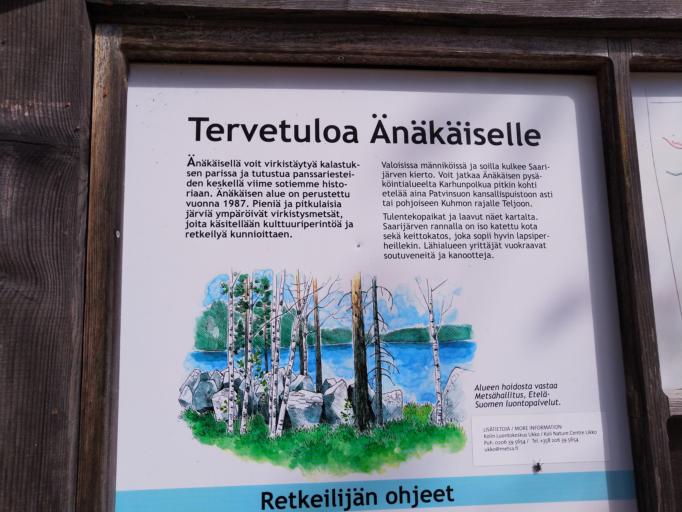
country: FI
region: North Karelia
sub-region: Pielisen Karjala
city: Lieksa
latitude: 63.5690
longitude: 30.0979
